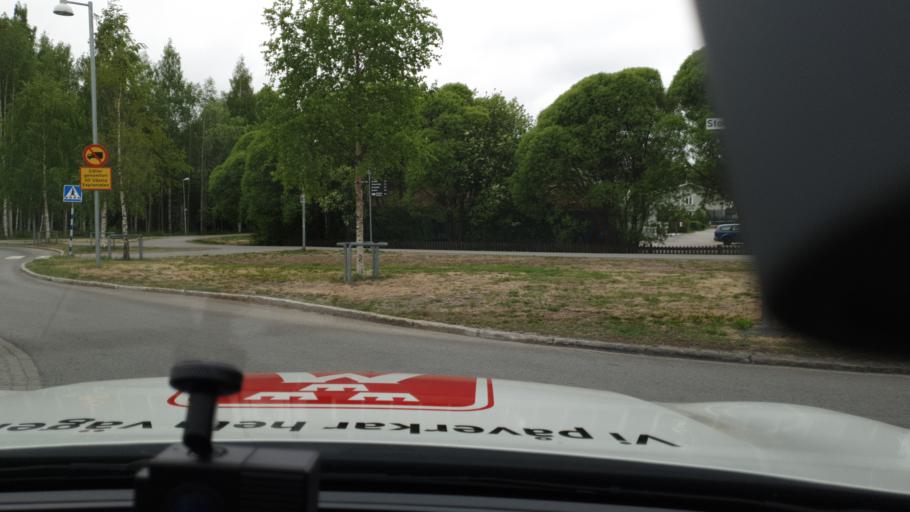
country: SE
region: Vaesterbotten
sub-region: Umea Kommun
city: Umea
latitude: 63.8321
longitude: 20.2266
